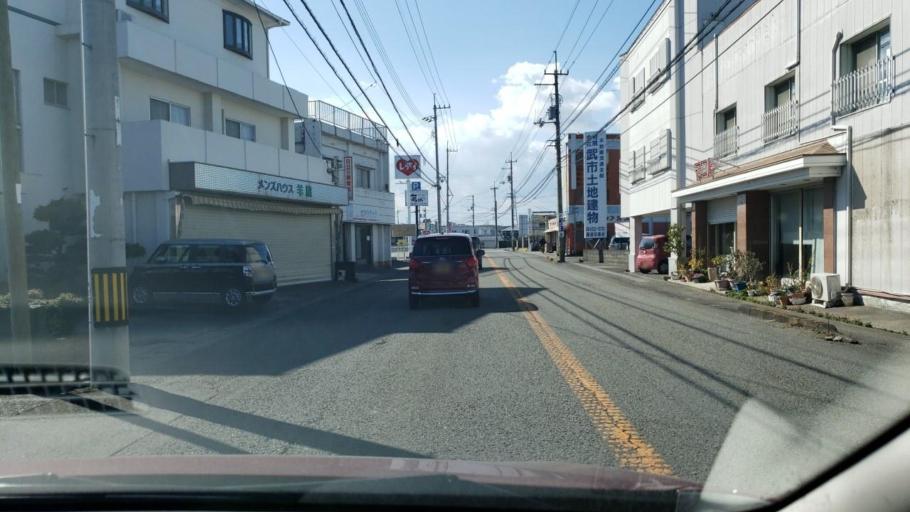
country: JP
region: Tokushima
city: Ishii
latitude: 34.1350
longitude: 134.4935
